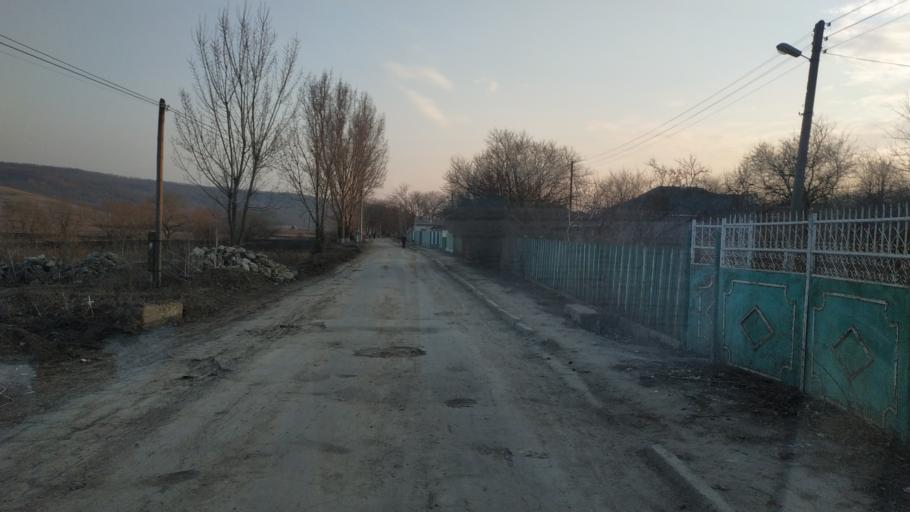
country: MD
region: Hincesti
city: Dancu
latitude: 46.7085
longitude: 28.3451
